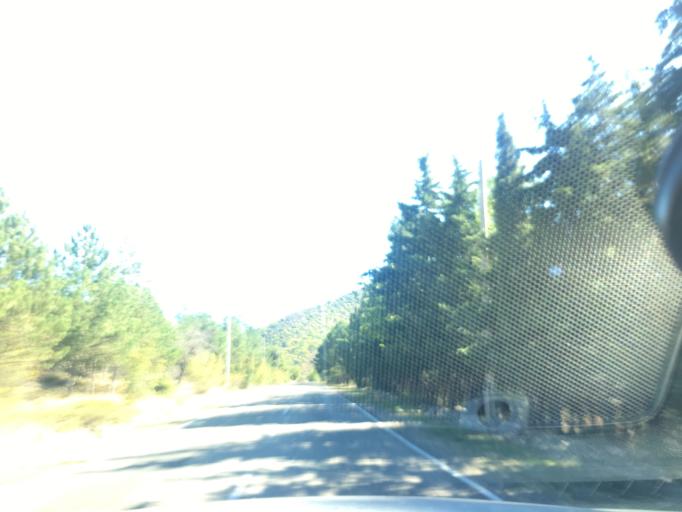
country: GE
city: Zahesi
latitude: 41.8316
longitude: 44.8589
